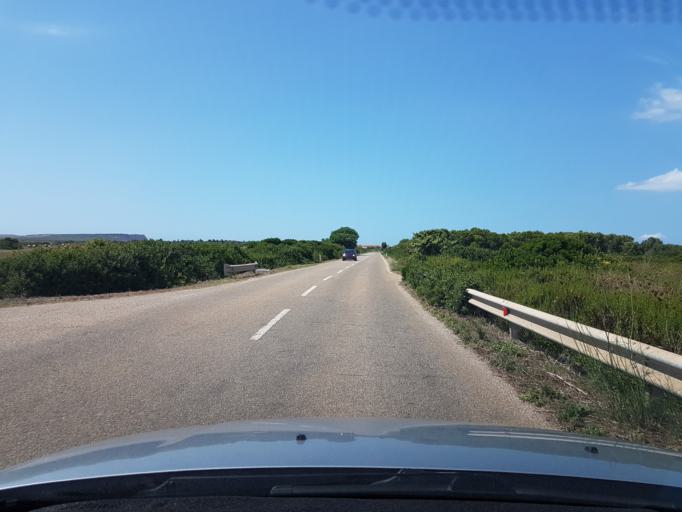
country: IT
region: Sardinia
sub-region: Provincia di Oristano
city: Riola Sardo
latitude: 40.0343
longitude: 8.4233
